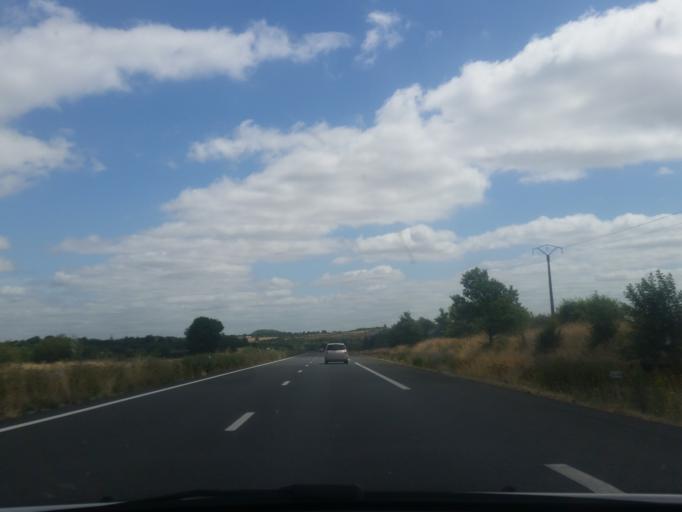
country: FR
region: Pays de la Loire
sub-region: Departement de Maine-et-Loire
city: Ingrandes
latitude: 47.4203
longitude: -0.9563
